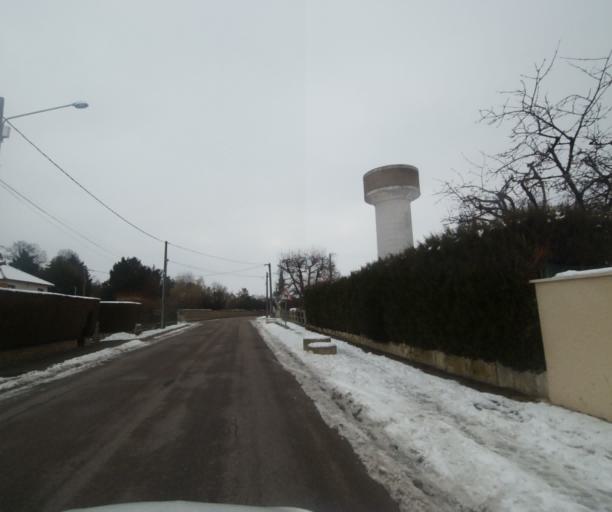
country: FR
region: Champagne-Ardenne
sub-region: Departement de la Haute-Marne
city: Villiers-en-Lieu
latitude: 48.5913
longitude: 4.8621
